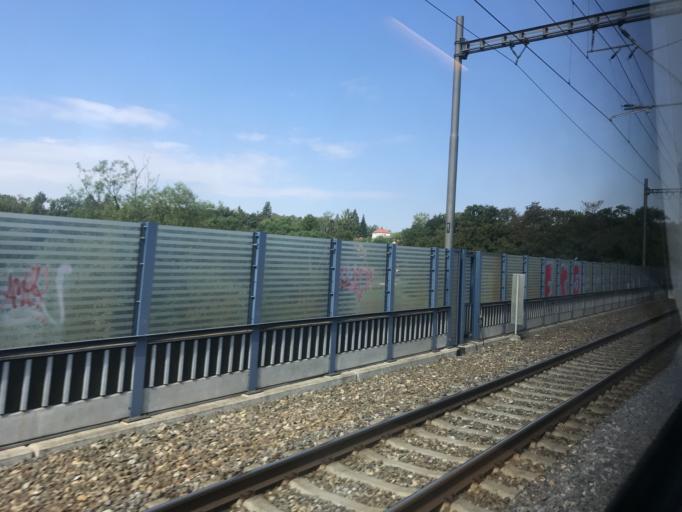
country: CZ
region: Central Bohemia
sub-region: Okres Benesov
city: Cercany
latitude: 49.8544
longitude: 14.6998
